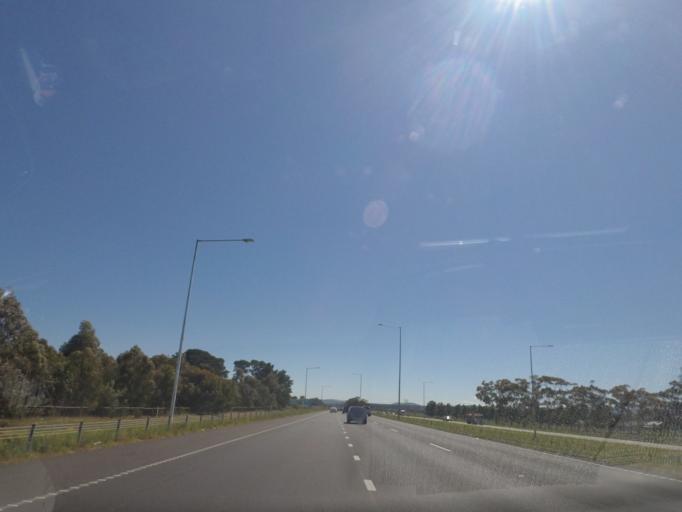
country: AU
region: Victoria
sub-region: Hume
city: Craigieburn
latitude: -37.5654
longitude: 144.9413
